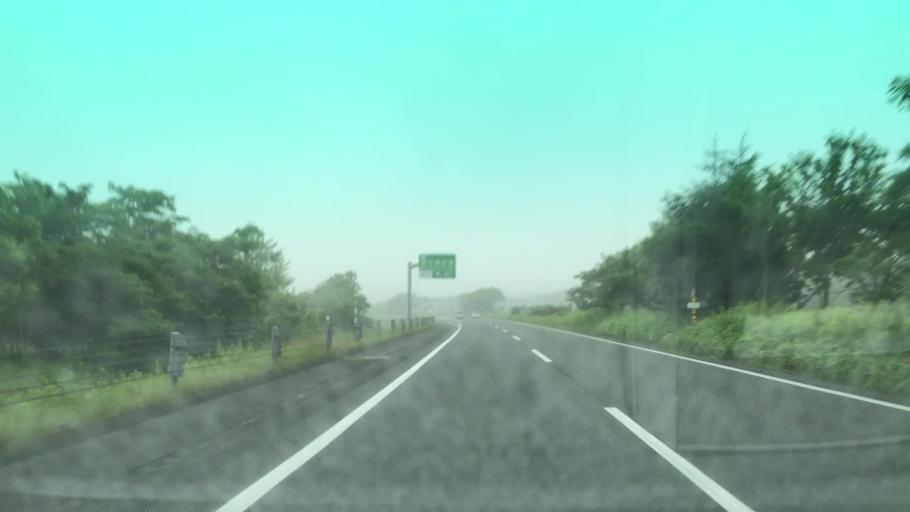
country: JP
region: Hokkaido
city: Chitose
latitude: 42.7805
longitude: 141.6270
